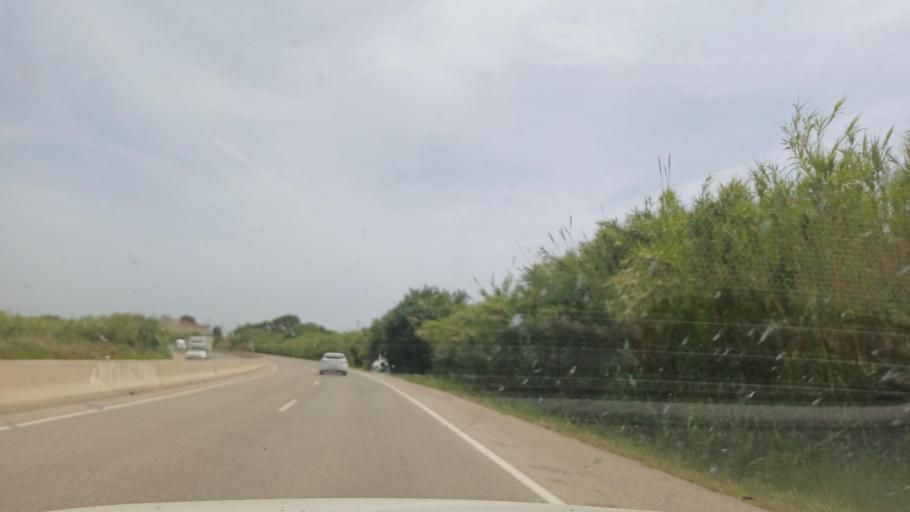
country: ES
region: Catalonia
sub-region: Provincia de Tarragona
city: Vila-seca
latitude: 41.1310
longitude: 1.1462
